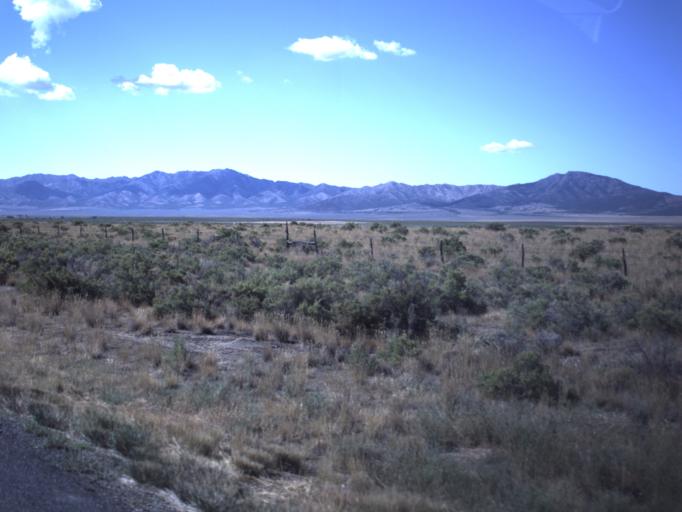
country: US
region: Utah
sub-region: Tooele County
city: Tooele
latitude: 40.1414
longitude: -112.4308
